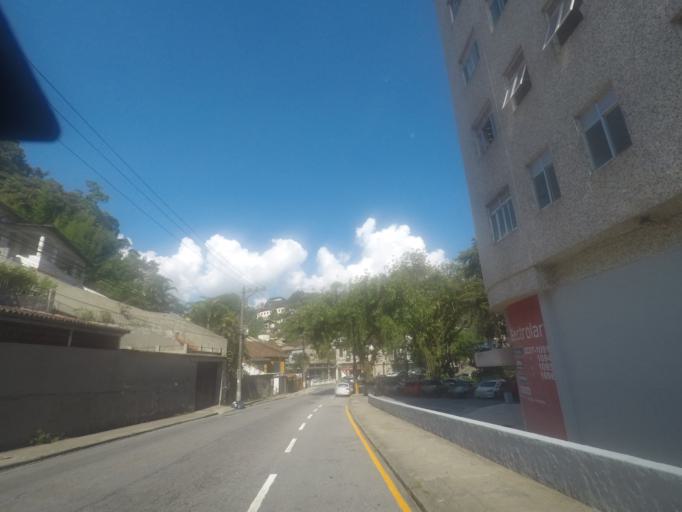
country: BR
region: Rio de Janeiro
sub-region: Petropolis
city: Petropolis
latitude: -22.5207
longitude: -43.1892
